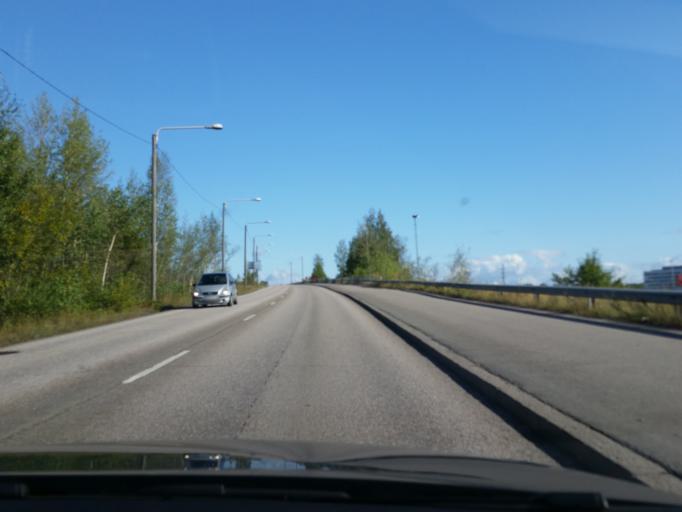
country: FI
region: Uusimaa
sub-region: Helsinki
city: Helsinki
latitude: 60.2146
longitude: 24.9331
